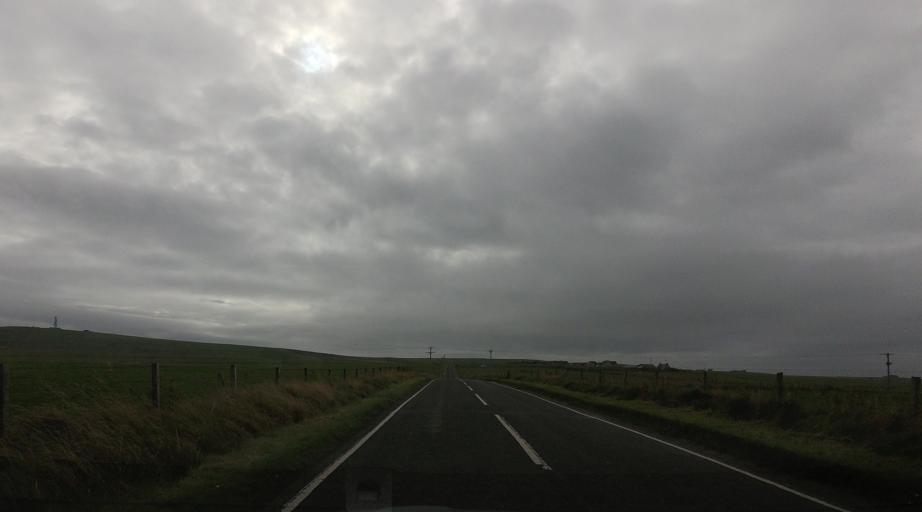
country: GB
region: Scotland
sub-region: Orkney Islands
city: Orkney
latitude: 58.7903
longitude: -2.9593
